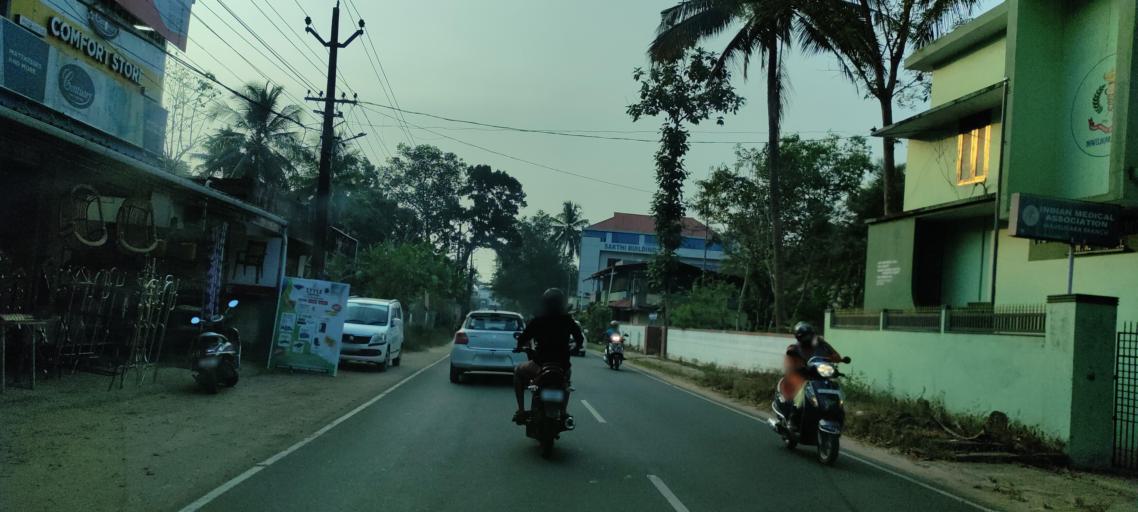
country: IN
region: Kerala
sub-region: Alappuzha
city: Mavelikara
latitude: 9.2550
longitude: 76.5603
